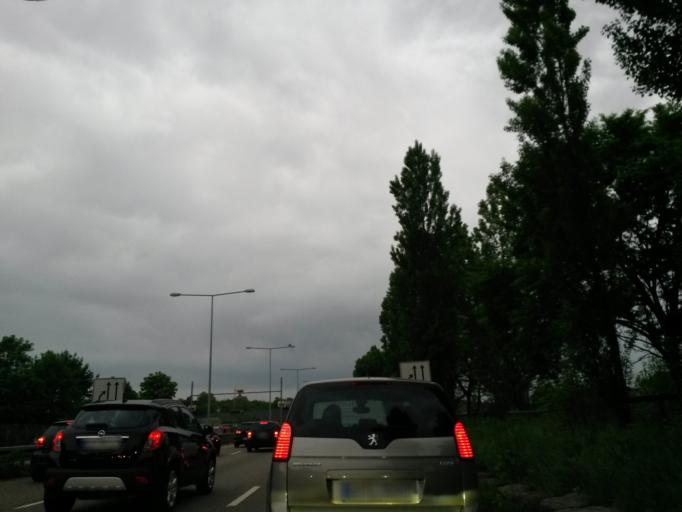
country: DE
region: Baden-Wuerttemberg
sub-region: Regierungsbezirk Stuttgart
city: Stuttgart-Ost
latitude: 48.7953
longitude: 9.2152
